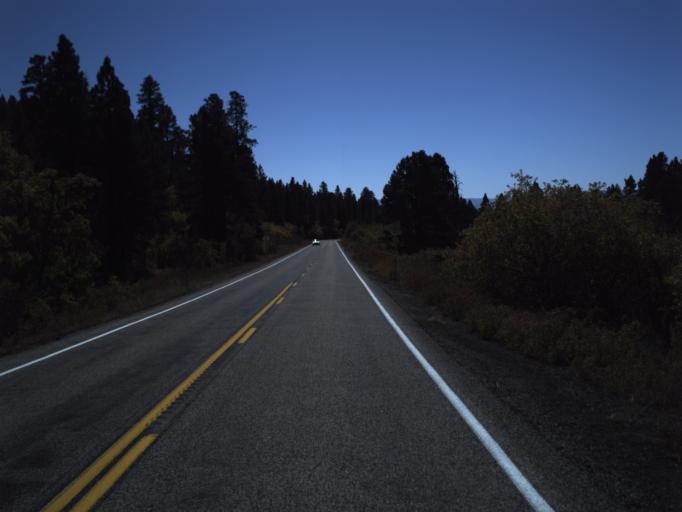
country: US
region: Utah
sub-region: Wayne County
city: Loa
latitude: 37.9930
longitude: -111.4300
